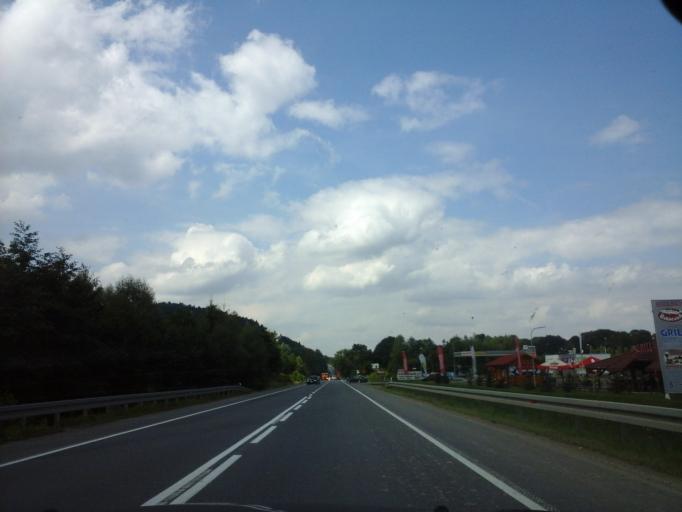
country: PL
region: Lesser Poland Voivodeship
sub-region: Powiat wadowicki
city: Jaroszowice
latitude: 49.8053
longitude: 19.5450
